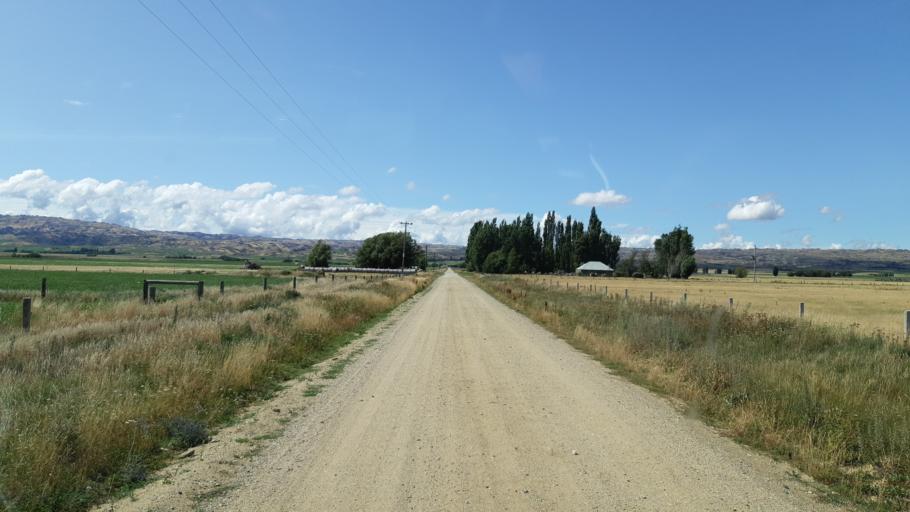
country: NZ
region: Otago
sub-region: Queenstown-Lakes District
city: Wanaka
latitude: -45.2066
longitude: 169.6608
